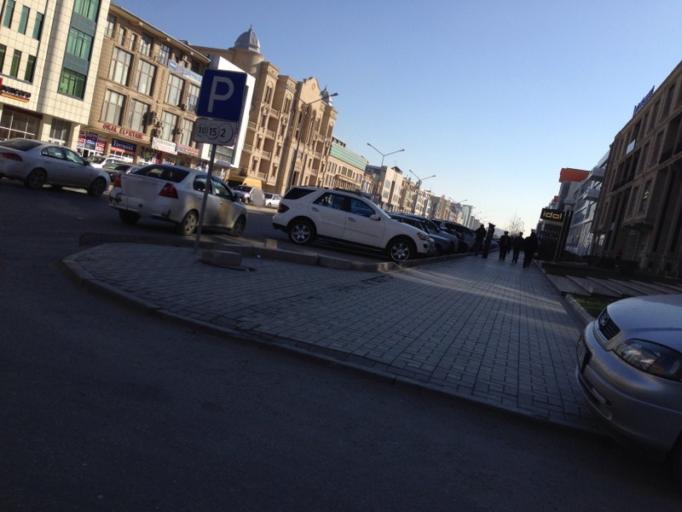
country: AZ
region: Baki
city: Baku
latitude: 40.4135
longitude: 49.8603
